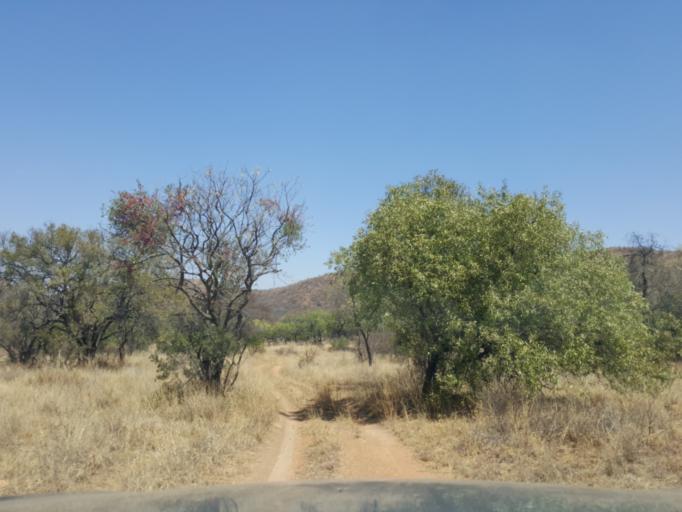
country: BW
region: South East
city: Lobatse
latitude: -25.1408
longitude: 25.6707
